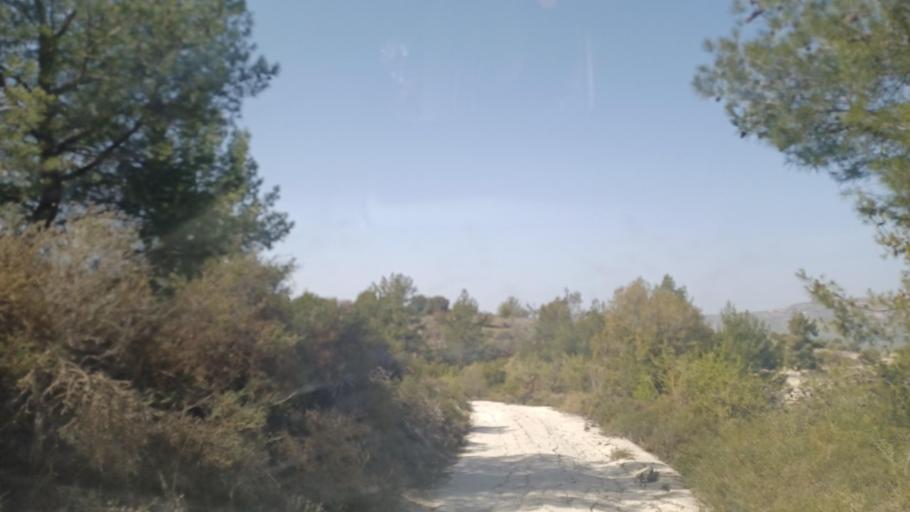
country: CY
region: Limassol
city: Pachna
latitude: 34.8792
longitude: 32.7057
